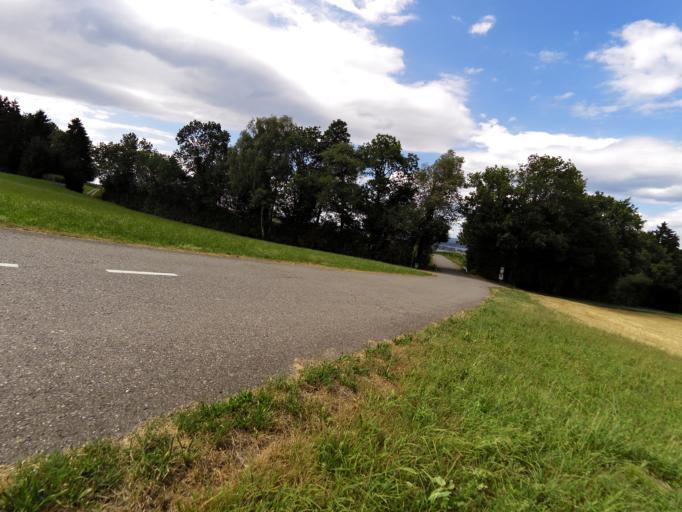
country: CH
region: Thurgau
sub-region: Kreuzlingen District
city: Tagerwilen
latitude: 47.6539
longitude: 9.1096
